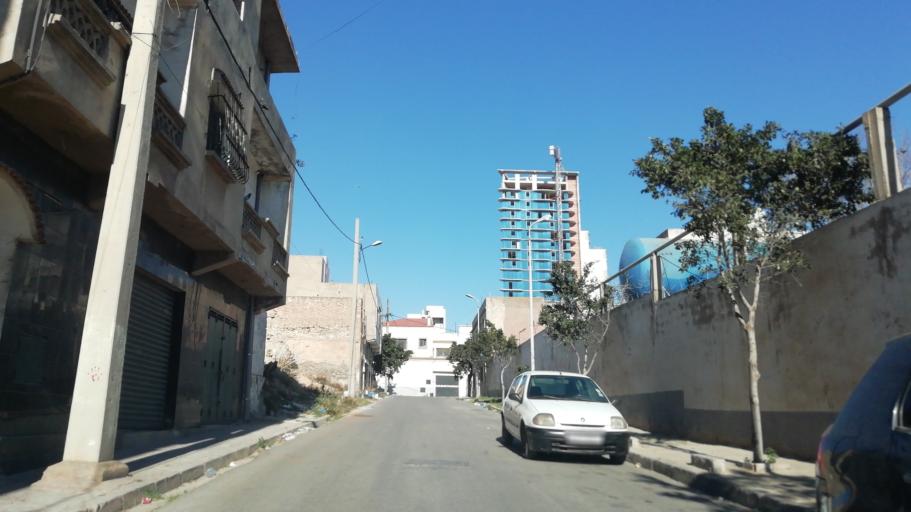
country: DZ
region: Oran
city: Oran
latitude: 35.7121
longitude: -0.6222
